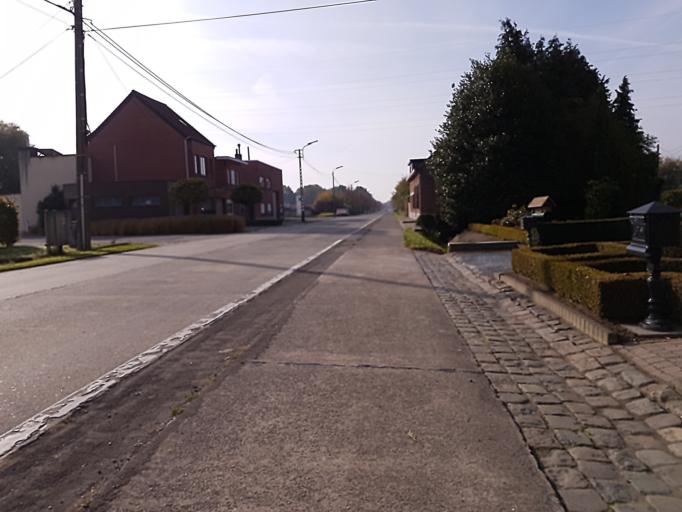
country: BE
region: Flanders
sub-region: Provincie Antwerpen
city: Sint-Katelijne-Waver
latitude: 51.0822
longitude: 4.5426
